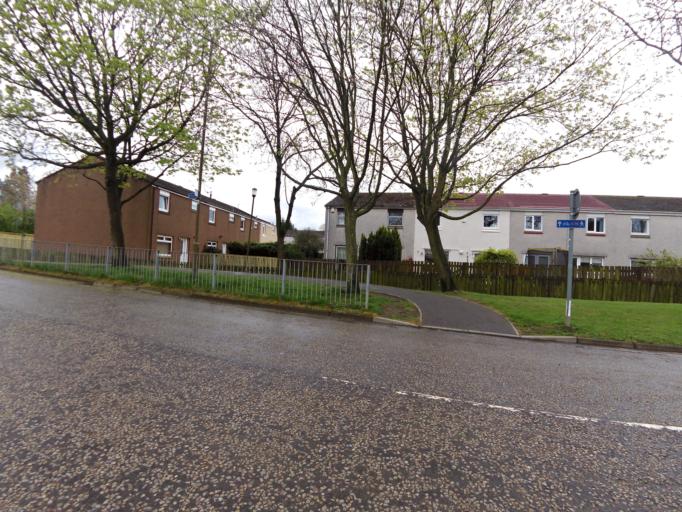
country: GB
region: Scotland
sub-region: Edinburgh
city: Queensferry
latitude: 55.9828
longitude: -3.3836
